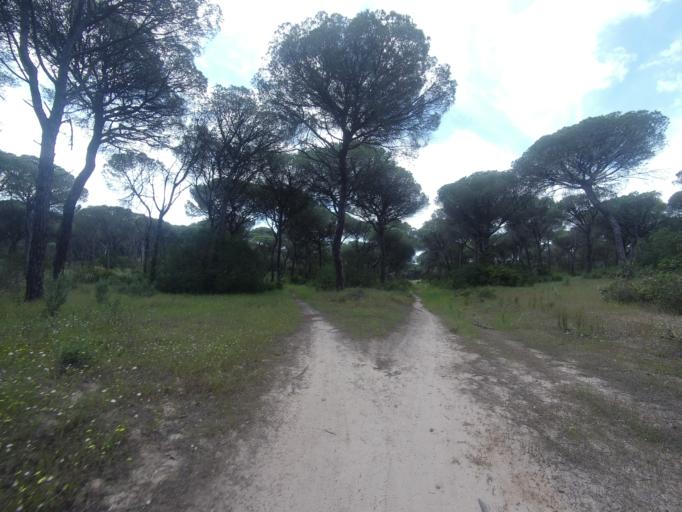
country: ES
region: Andalusia
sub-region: Provincia de Huelva
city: Aljaraque
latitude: 37.2257
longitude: -7.0683
